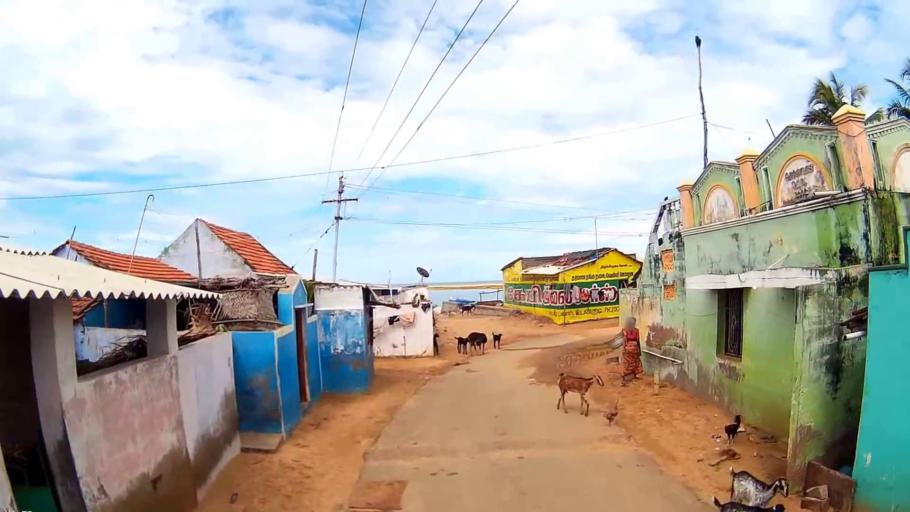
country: IN
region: Tamil Nadu
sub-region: Thoothukkudi
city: Udankudi
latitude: 8.3790
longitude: 78.0566
